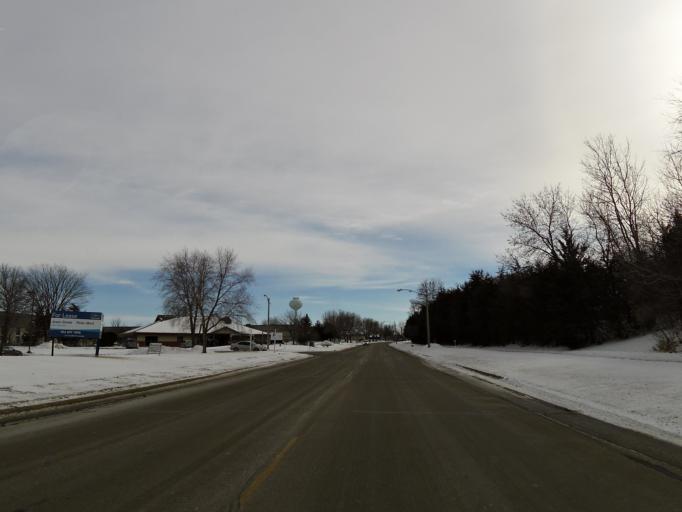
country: US
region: Wisconsin
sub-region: Saint Croix County
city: Hudson
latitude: 44.9580
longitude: -92.7417
